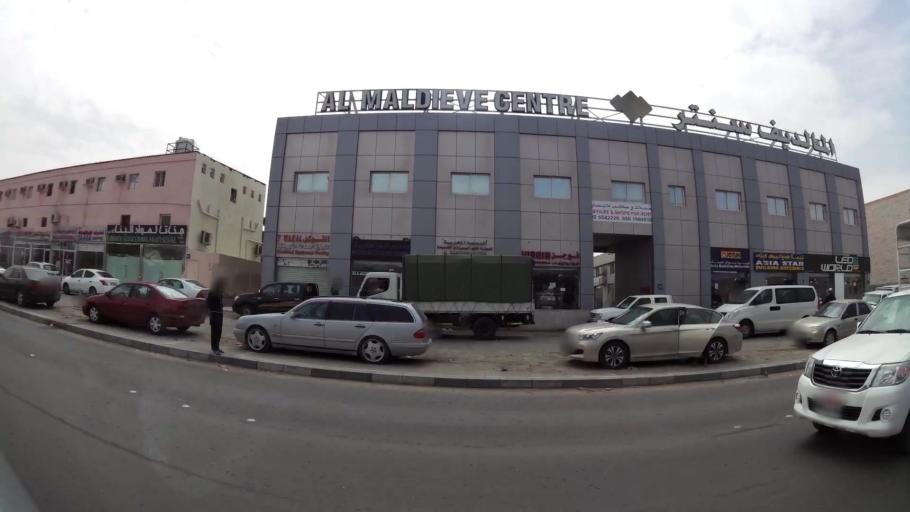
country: AE
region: Abu Dhabi
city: Abu Dhabi
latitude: 24.3728
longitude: 54.5033
